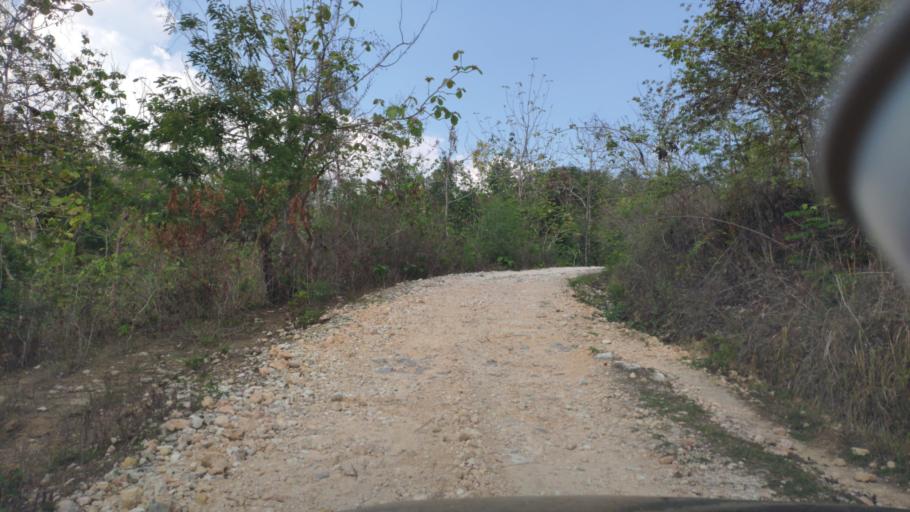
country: ID
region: Central Java
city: Semanggi
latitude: -7.0573
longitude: 111.4221
